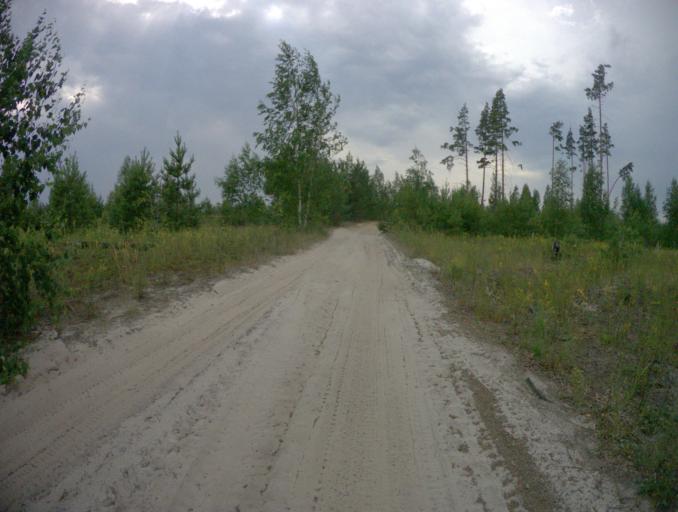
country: RU
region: Ivanovo
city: Talitsy
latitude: 56.4230
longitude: 42.3327
